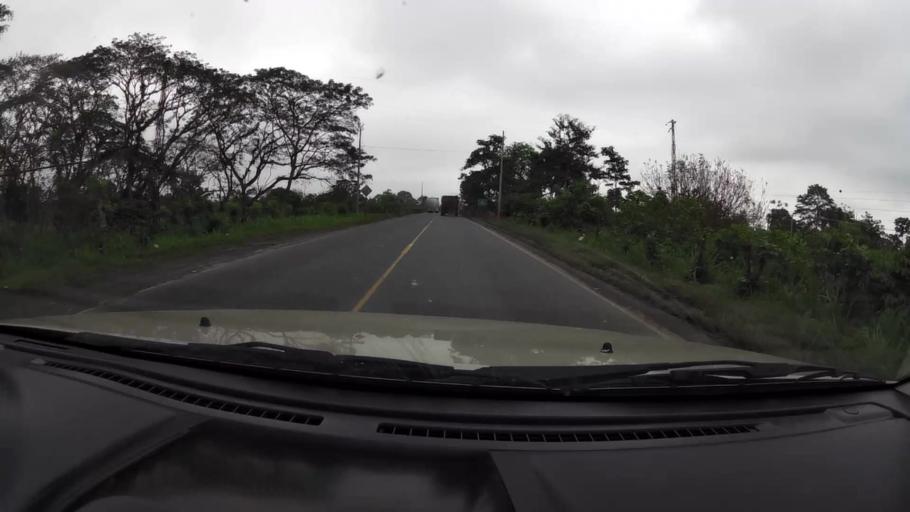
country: EC
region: Guayas
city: Balao
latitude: -3.0850
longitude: -79.7592
